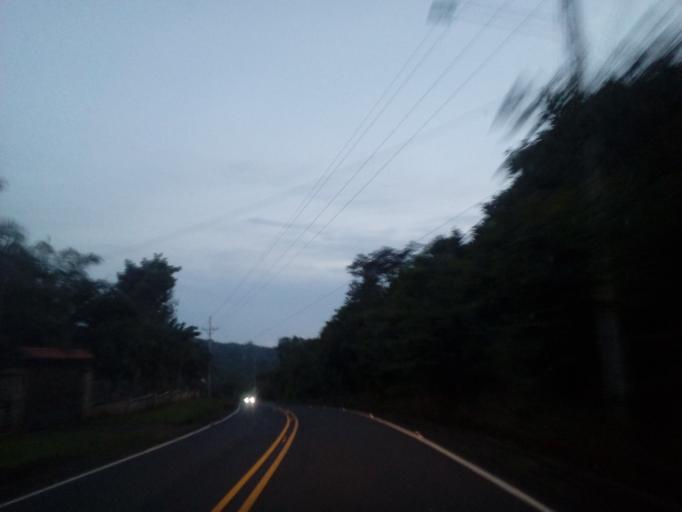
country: CR
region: Guanacaste
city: Samara
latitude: 9.9566
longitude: -85.5165
